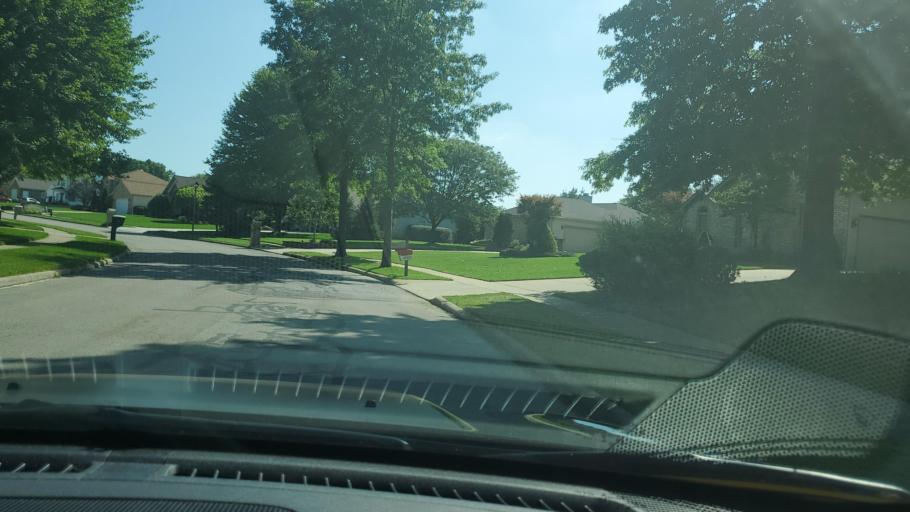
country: US
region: Ohio
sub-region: Trumbull County
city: Girard
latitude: 41.1736
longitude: -80.6962
